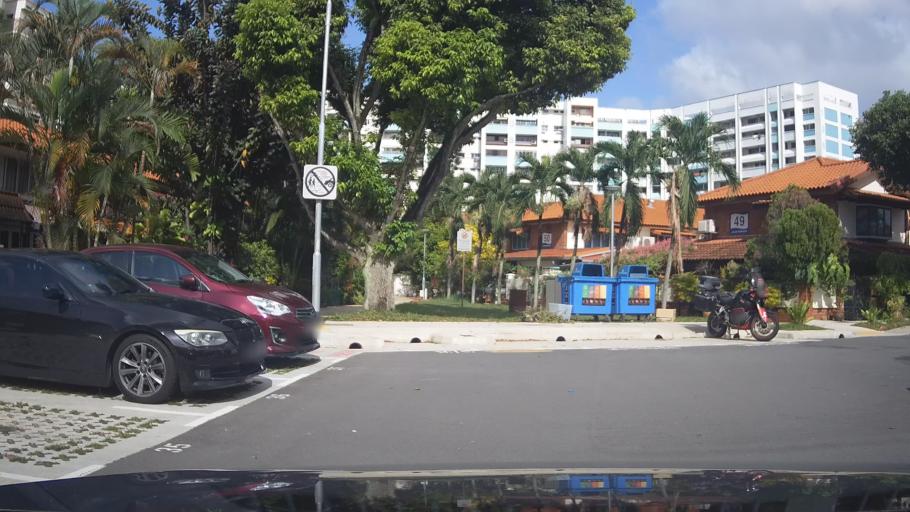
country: SG
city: Singapore
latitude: 1.3274
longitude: 103.8568
